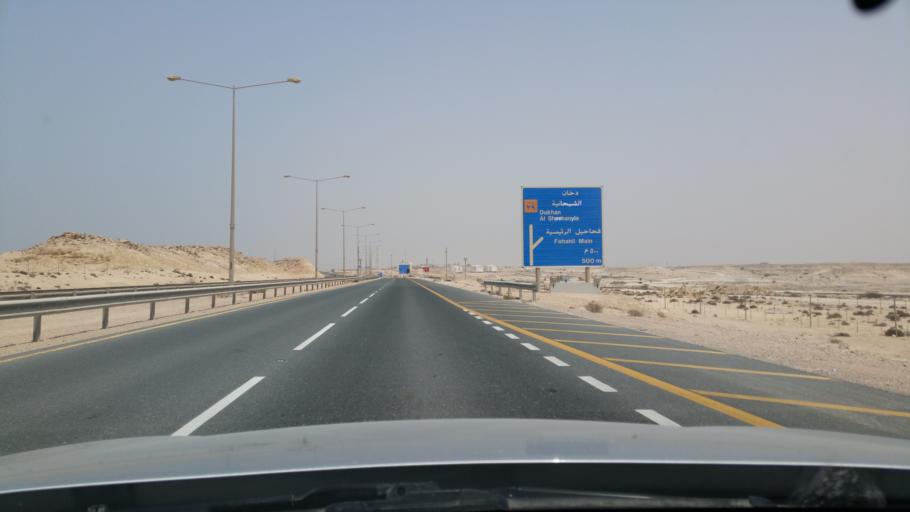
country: QA
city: Umm Bab
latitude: 25.2704
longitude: 50.7930
